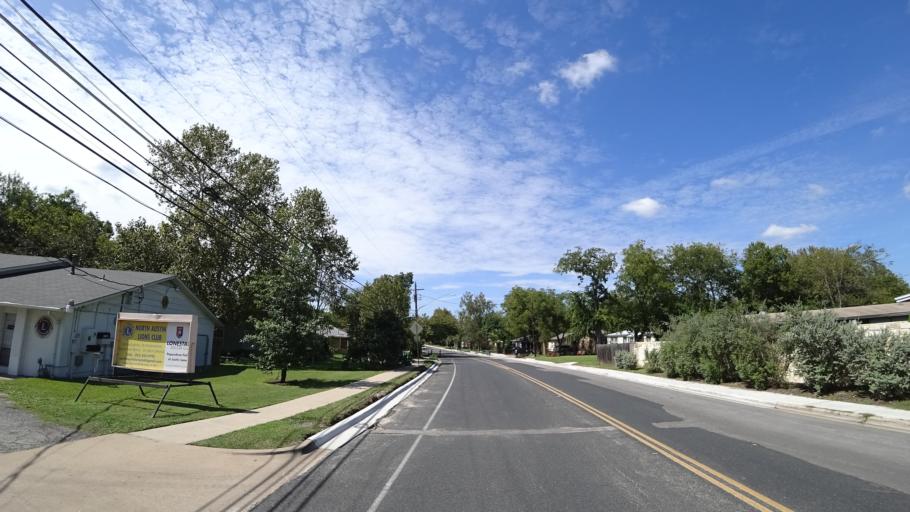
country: US
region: Texas
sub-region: Travis County
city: Austin
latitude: 30.3385
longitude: -97.7228
